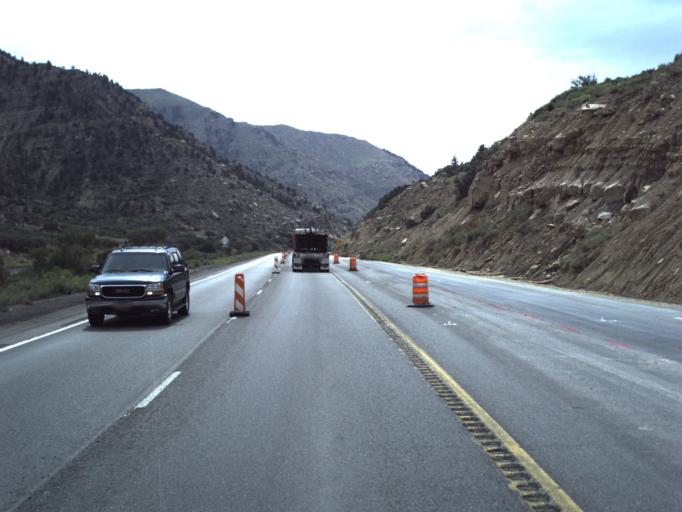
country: US
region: Utah
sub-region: Carbon County
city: Helper
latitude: 39.7852
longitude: -110.9266
